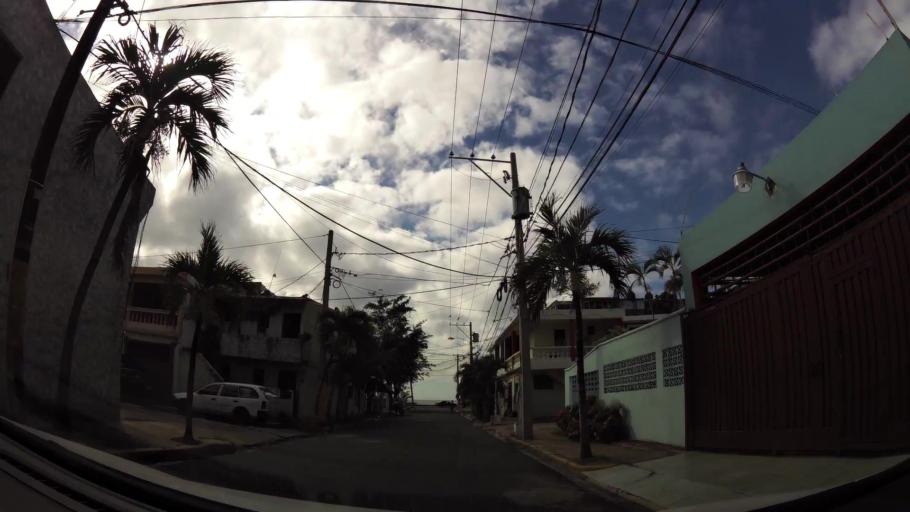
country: DO
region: Nacional
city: Bella Vista
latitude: 18.4437
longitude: -69.9287
